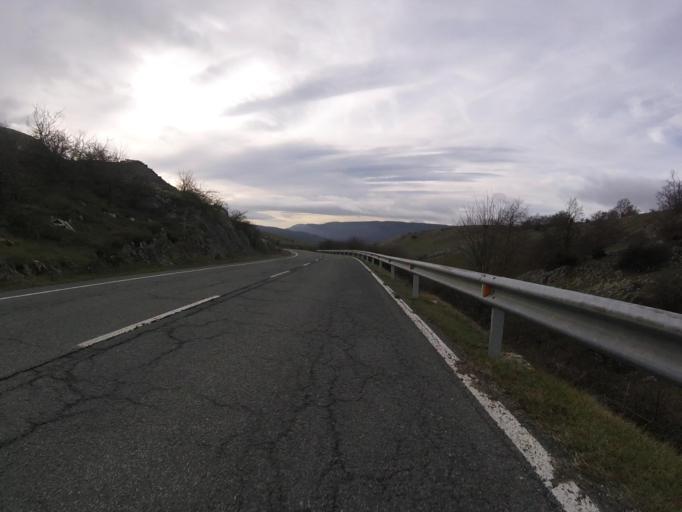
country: ES
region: Navarre
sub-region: Provincia de Navarra
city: Arbizu
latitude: 42.8576
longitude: -2.0127
